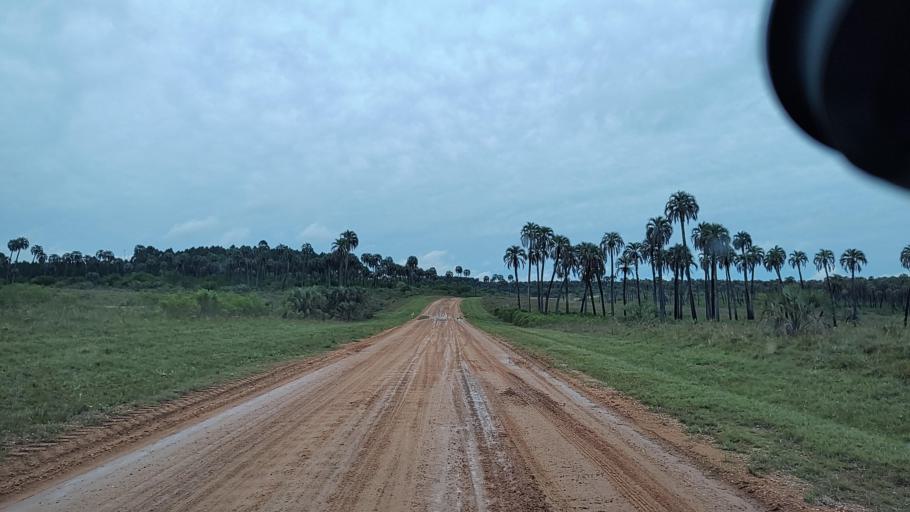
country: AR
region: Entre Rios
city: Ubajay
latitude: -31.8509
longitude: -58.3113
